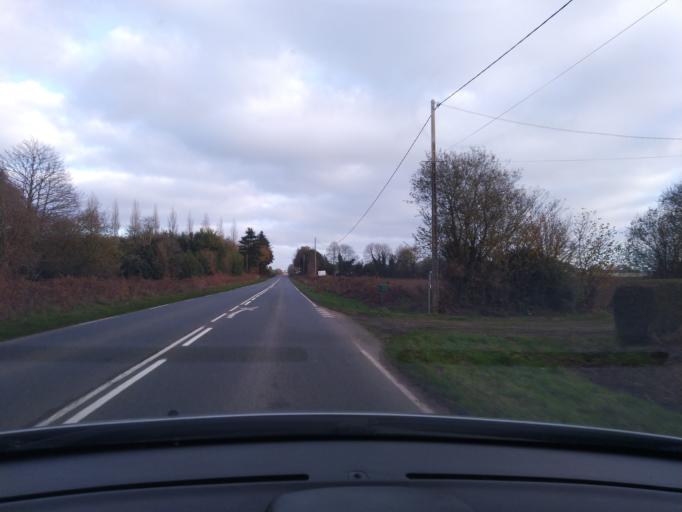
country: FR
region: Brittany
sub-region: Departement du Finistere
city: Plouigneau
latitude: 48.5730
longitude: -3.7380
